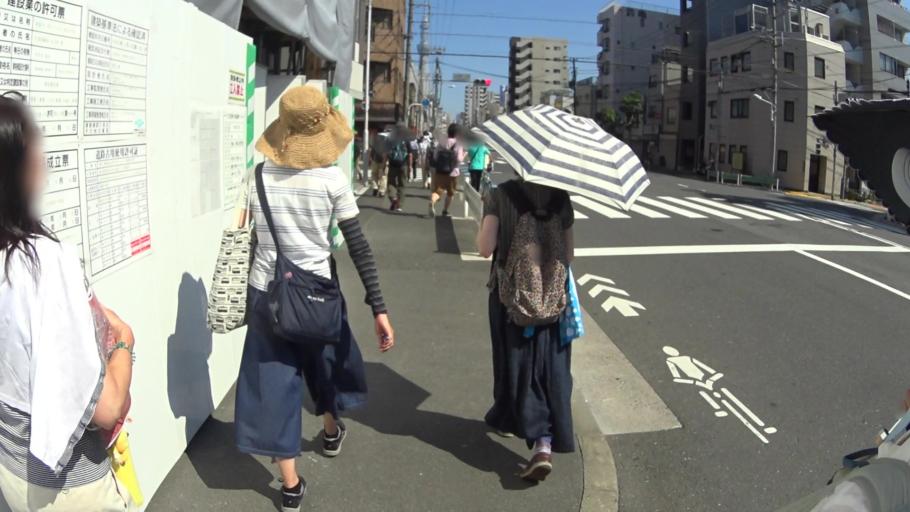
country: JP
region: Saitama
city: Soka
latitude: 35.7264
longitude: 139.7959
